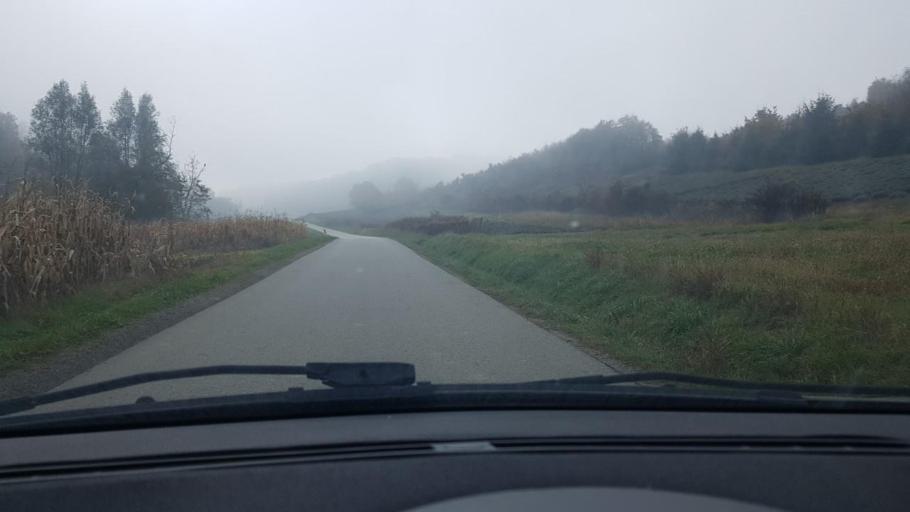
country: HR
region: Krapinsko-Zagorska
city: Zlatar
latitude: 46.1325
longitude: 16.0816
